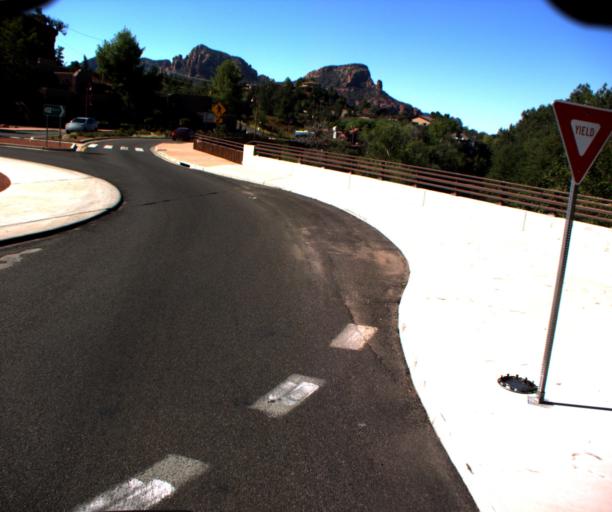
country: US
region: Arizona
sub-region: Coconino County
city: Sedona
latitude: 34.8621
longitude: -111.7618
